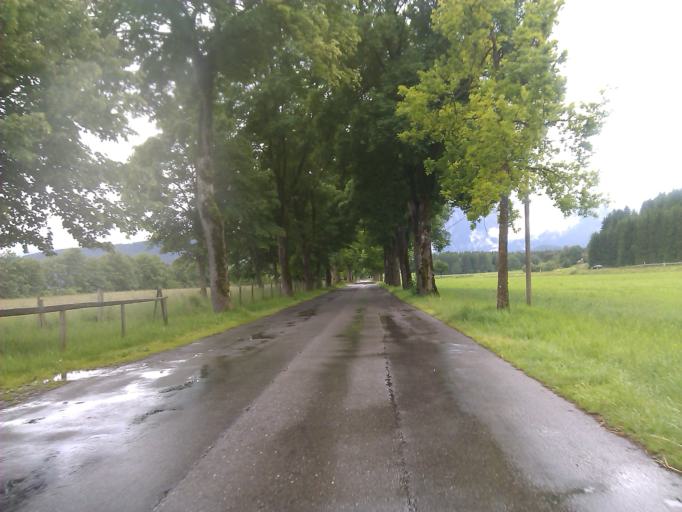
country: DE
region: Bavaria
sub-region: Swabia
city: Fuessen
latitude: 47.5974
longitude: 10.7123
